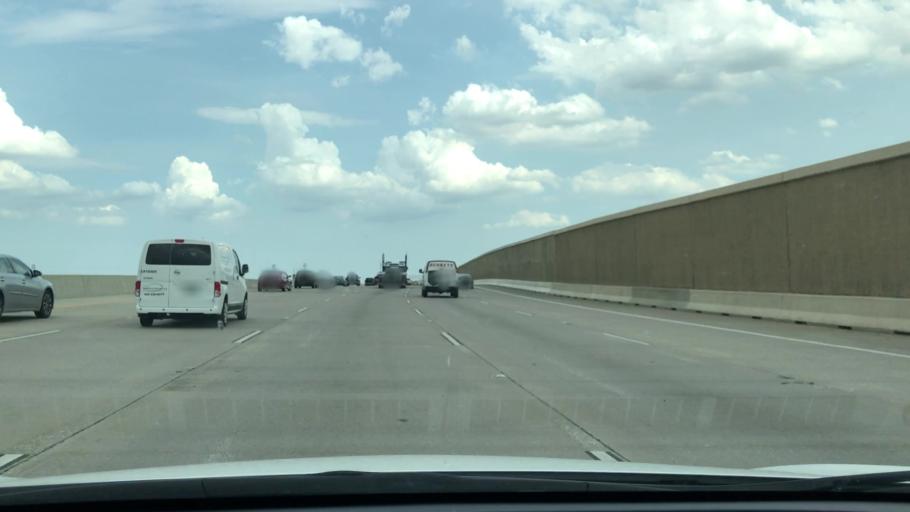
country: US
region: Texas
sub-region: Dallas County
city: Addison
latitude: 33.0092
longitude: -96.7859
